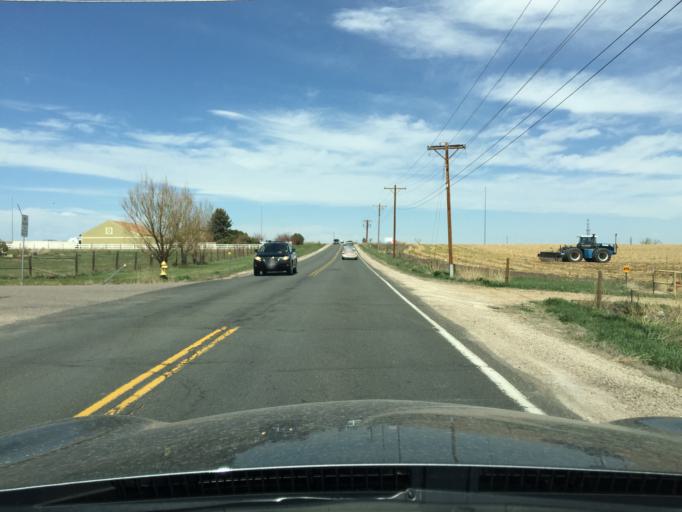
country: US
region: Colorado
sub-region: Boulder County
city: Erie
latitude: 39.9791
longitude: -104.9972
